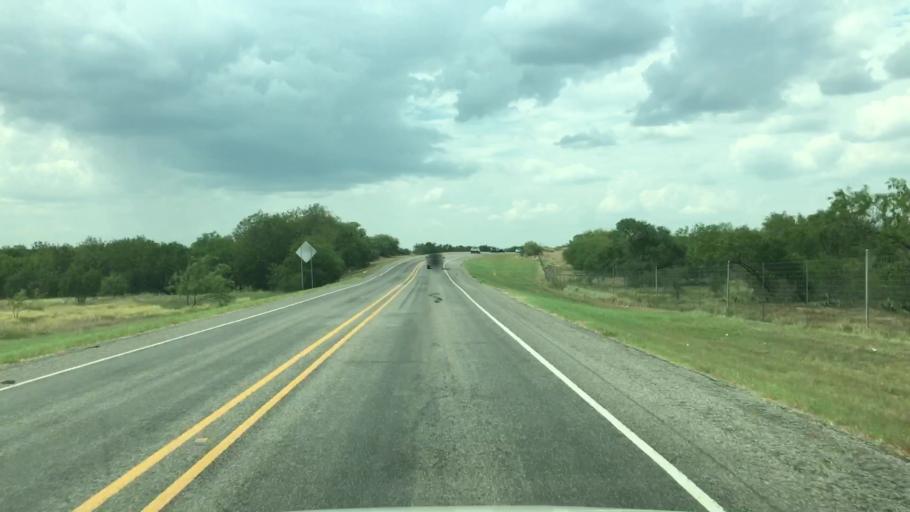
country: US
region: Texas
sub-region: Live Oak County
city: Three Rivers
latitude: 28.6400
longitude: -98.2809
